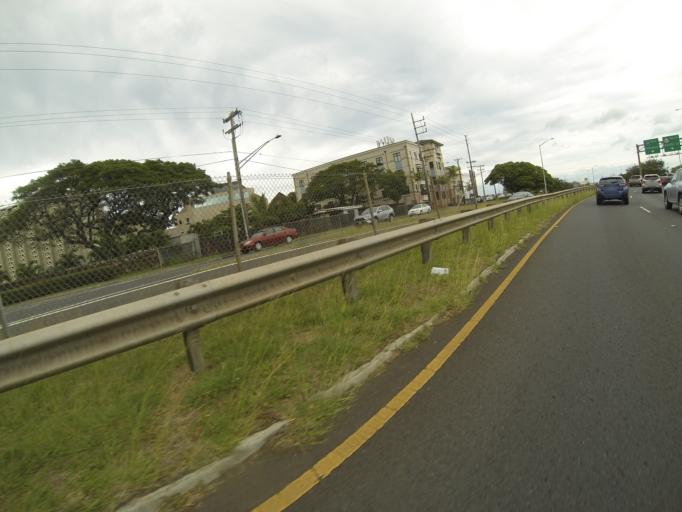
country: US
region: Hawaii
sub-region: Honolulu County
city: Honolulu
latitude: 21.3342
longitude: -157.8718
